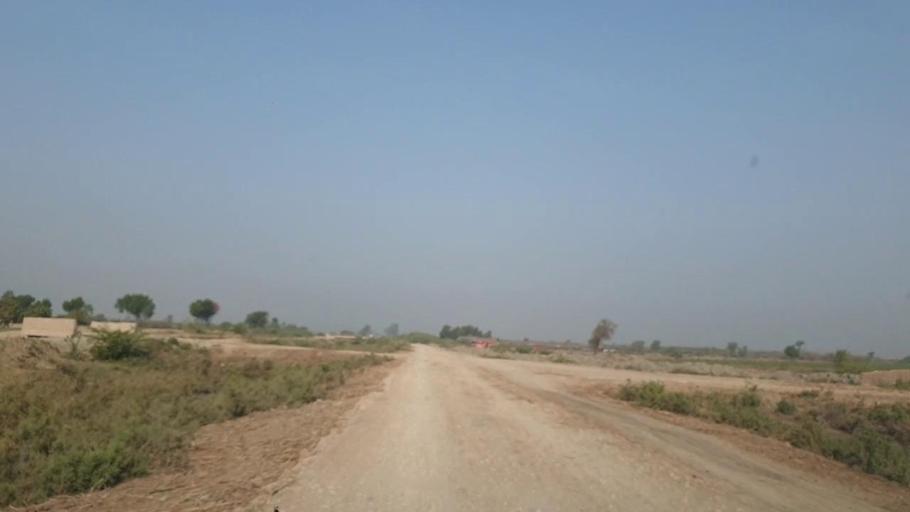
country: PK
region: Sindh
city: Mirpur Khas
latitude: 25.5574
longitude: 69.0151
